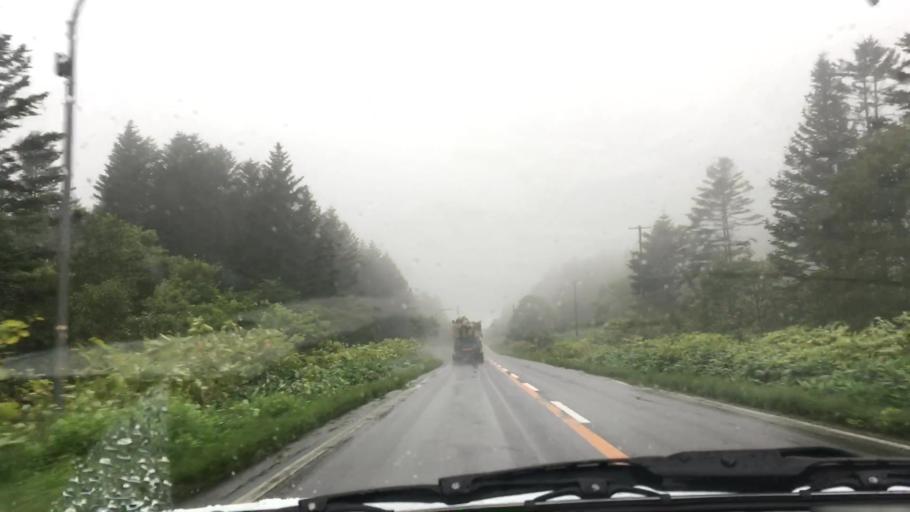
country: JP
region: Hokkaido
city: Niseko Town
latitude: 42.5946
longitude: 140.5089
